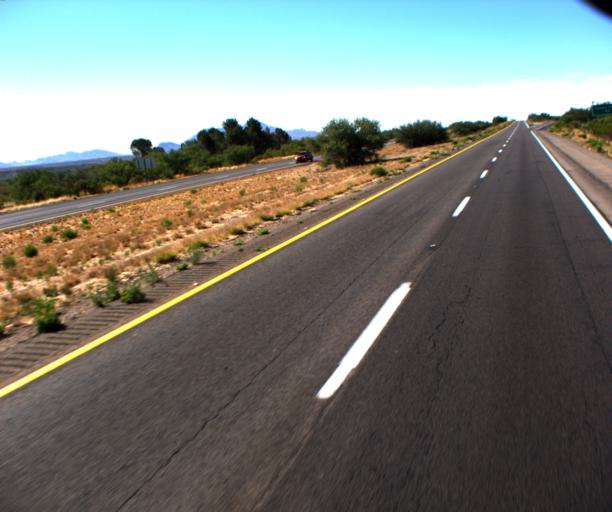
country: US
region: Arizona
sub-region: Santa Cruz County
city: Tubac
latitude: 31.6588
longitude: -111.0610
